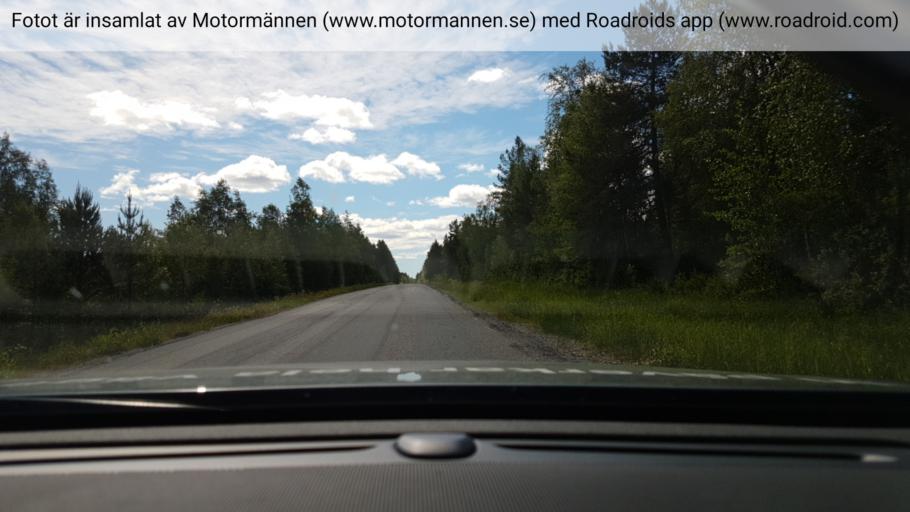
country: SE
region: Vaesterbotten
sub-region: Skelleftea Kommun
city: Burea
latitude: 64.4358
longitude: 21.3540
